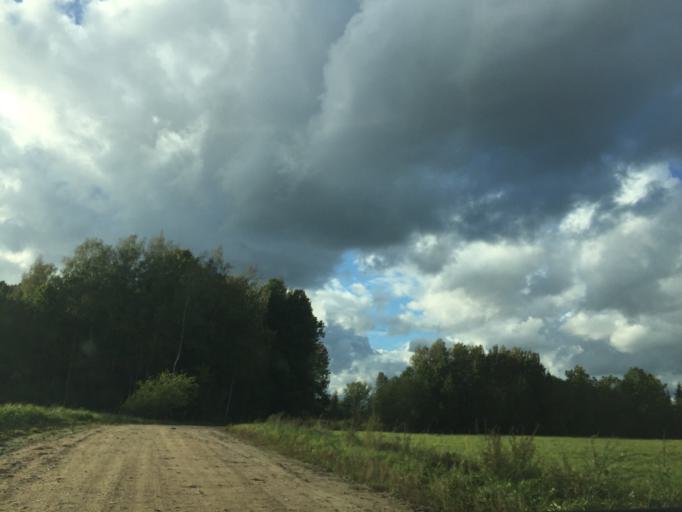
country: LV
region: Ligatne
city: Ligatne
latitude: 57.1379
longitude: 25.0848
